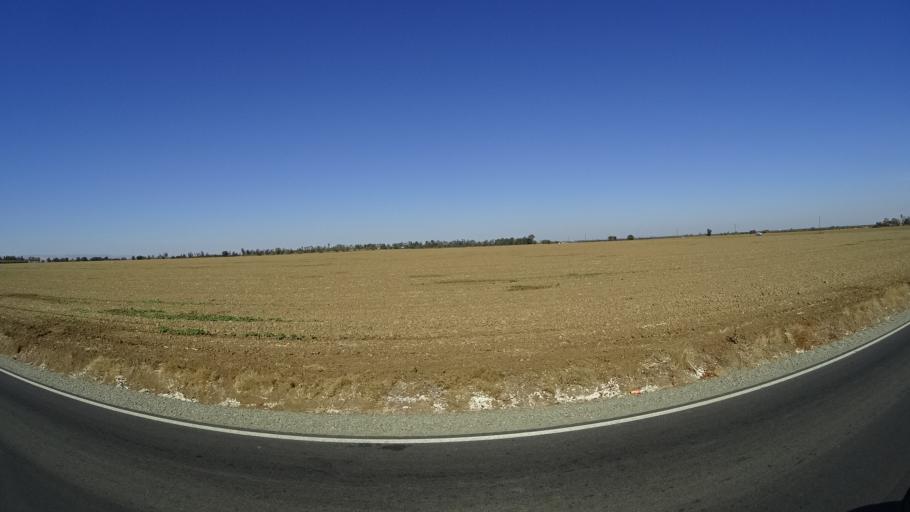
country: US
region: California
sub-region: Yolo County
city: Woodland
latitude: 38.6197
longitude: -121.8609
